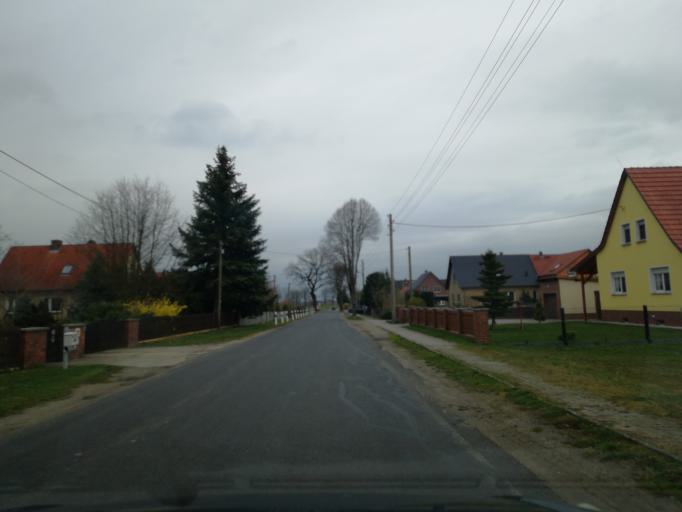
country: DE
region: Brandenburg
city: Calau
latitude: 51.7299
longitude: 14.0212
